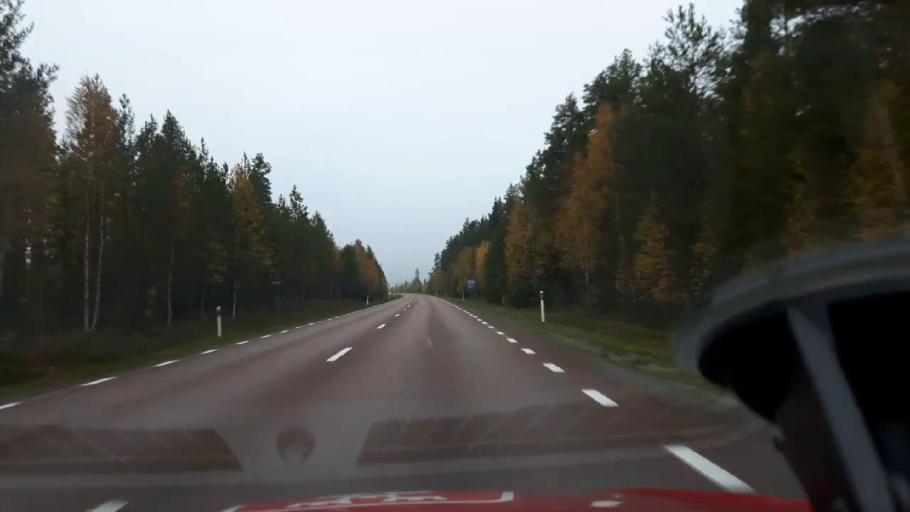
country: SE
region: Jaemtland
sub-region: Bergs Kommun
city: Hoverberg
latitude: 62.5382
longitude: 14.4489
